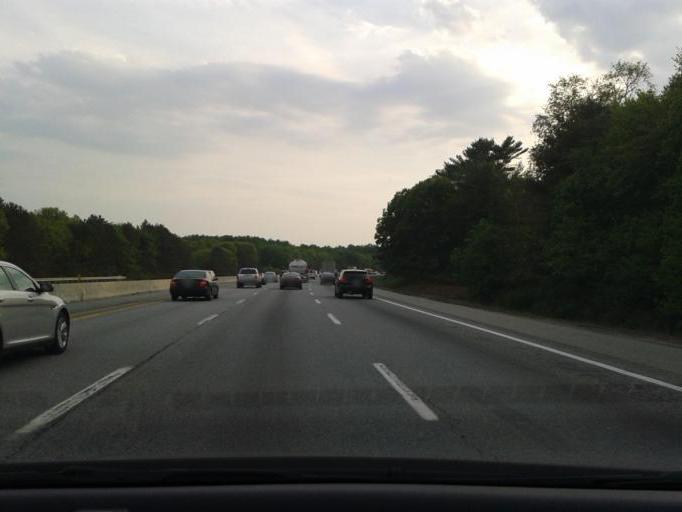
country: US
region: Massachusetts
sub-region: Middlesex County
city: Cochituate
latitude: 42.3201
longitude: -71.3427
